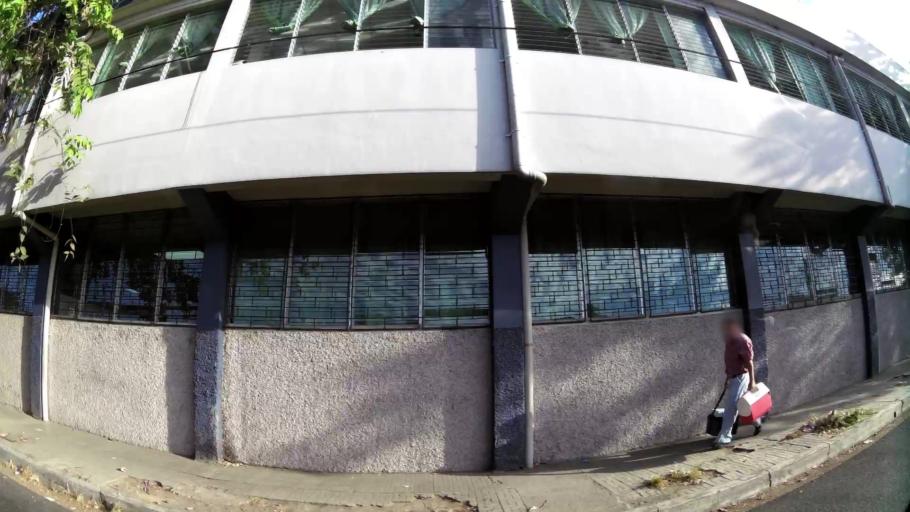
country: SV
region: Santa Ana
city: Santa Ana
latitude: 13.9974
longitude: -89.5612
